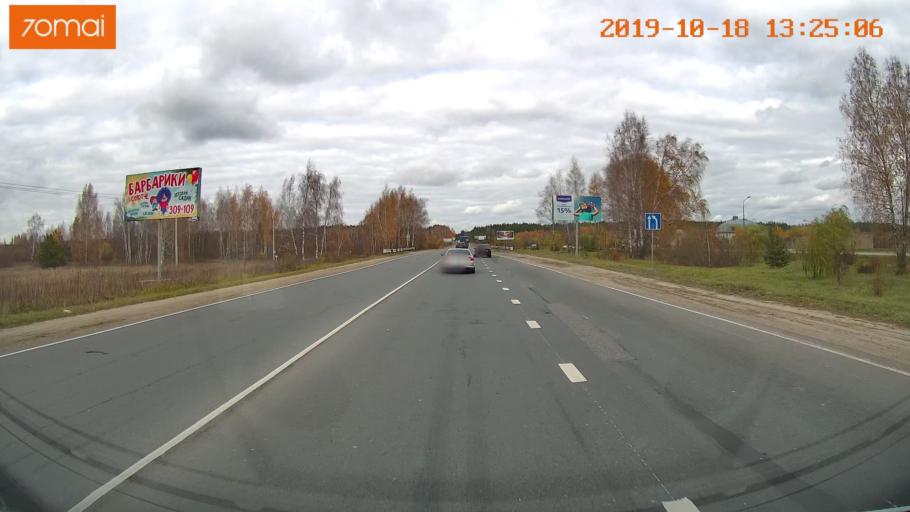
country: RU
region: Rjazan
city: Polyany
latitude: 54.7398
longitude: 39.8409
